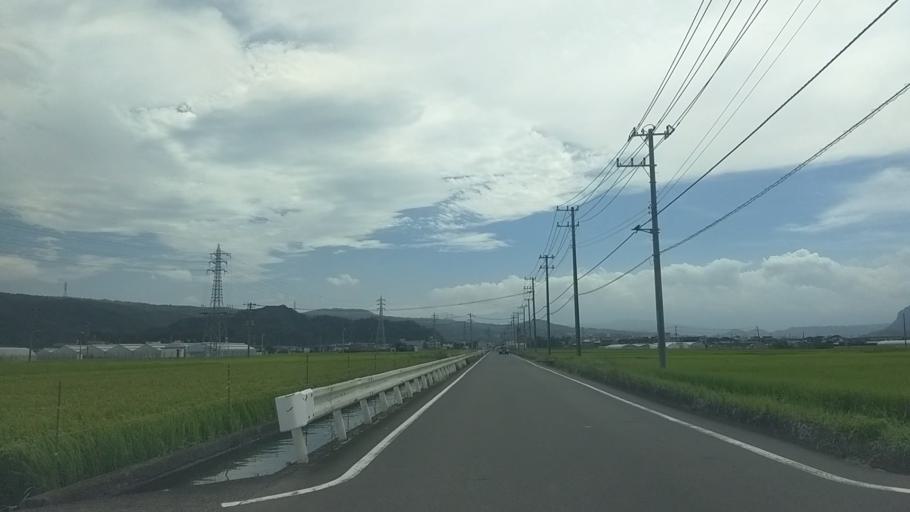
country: JP
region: Shizuoka
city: Mishima
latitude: 35.0643
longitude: 138.9465
